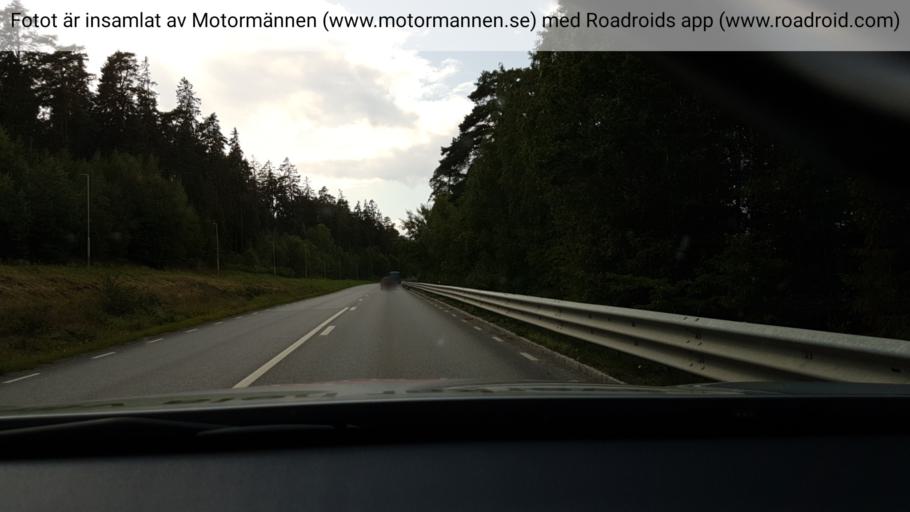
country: SE
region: Stockholm
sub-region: Ekero Kommun
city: Ekeroe
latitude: 59.3026
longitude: 17.8017
